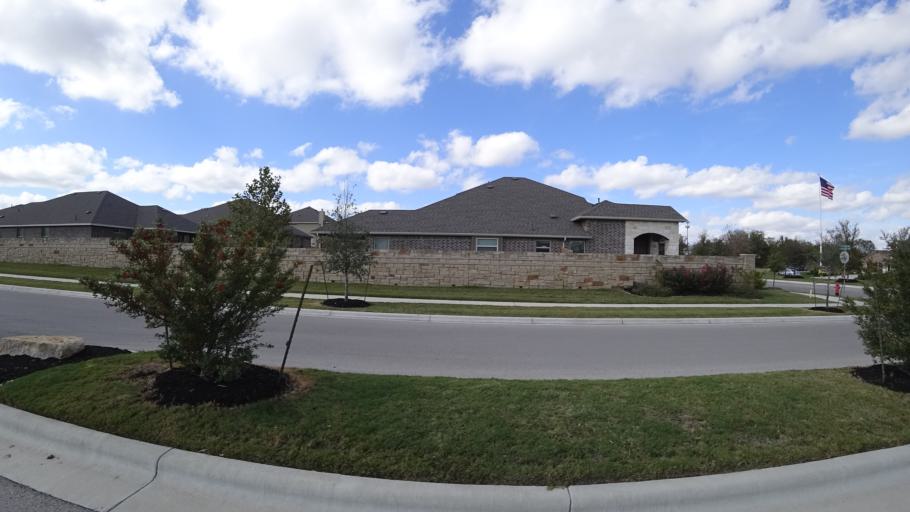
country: US
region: Texas
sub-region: Travis County
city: Windemere
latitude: 30.4794
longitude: -97.6535
